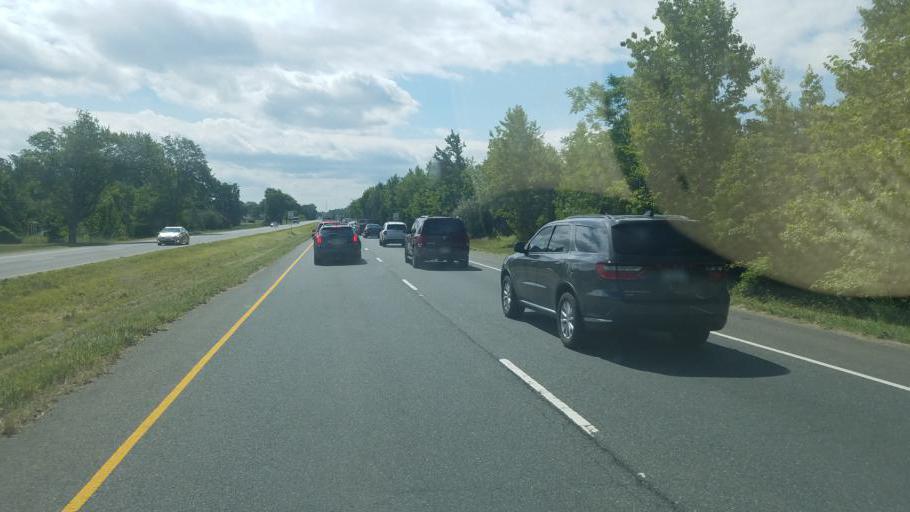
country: US
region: Virginia
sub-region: Stafford County
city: Falmouth
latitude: 38.3790
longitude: -77.5376
